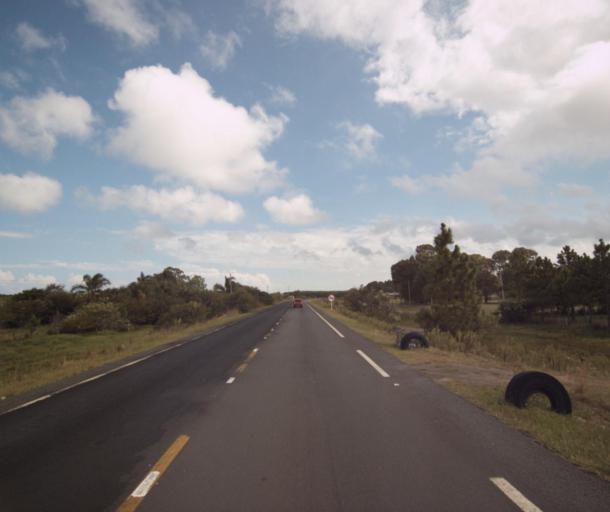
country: BR
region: Rio Grande do Sul
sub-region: Tapes
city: Tapes
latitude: -31.4086
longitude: -51.1678
